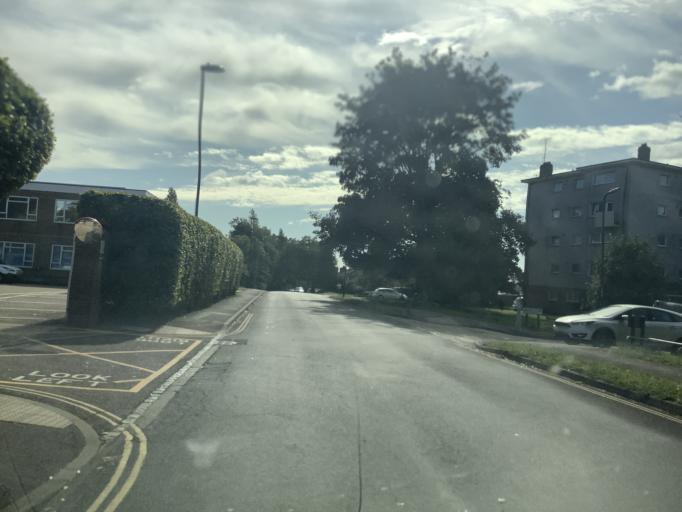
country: GB
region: England
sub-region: Hampshire
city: Marchwood
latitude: 50.9265
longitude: -1.4485
